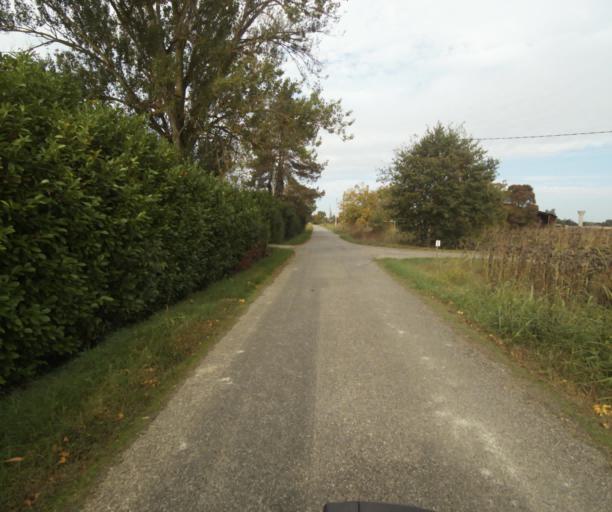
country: FR
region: Midi-Pyrenees
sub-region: Departement du Tarn-et-Garonne
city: Finhan
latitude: 43.9071
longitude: 1.2305
